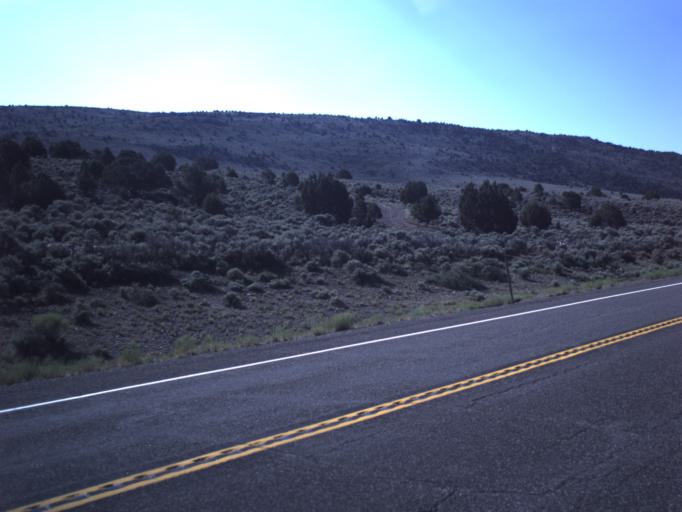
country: US
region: Utah
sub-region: Wayne County
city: Loa
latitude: 38.5037
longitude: -111.8328
